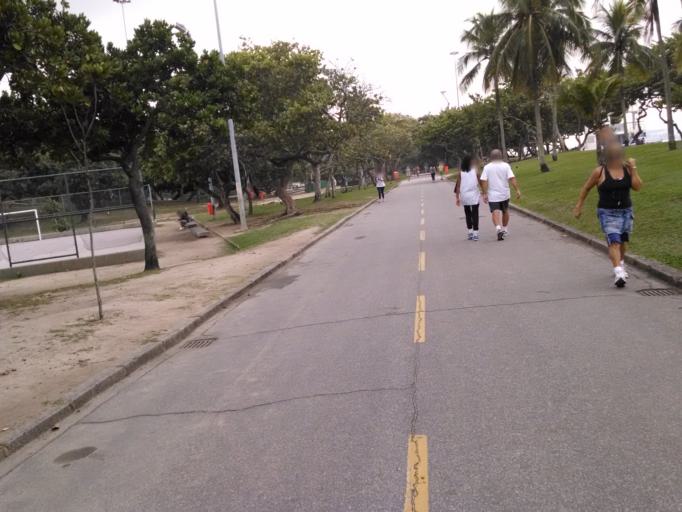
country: BR
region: Rio de Janeiro
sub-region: Rio De Janeiro
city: Rio de Janeiro
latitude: -22.9279
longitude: -43.1713
